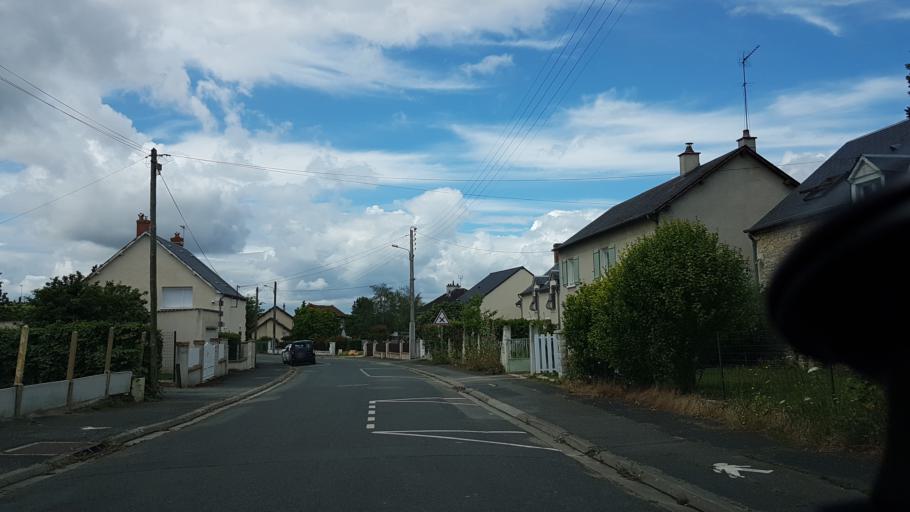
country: FR
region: Centre
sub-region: Departement du Cher
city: Saint-Doulchard
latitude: 47.1055
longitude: 2.3563
